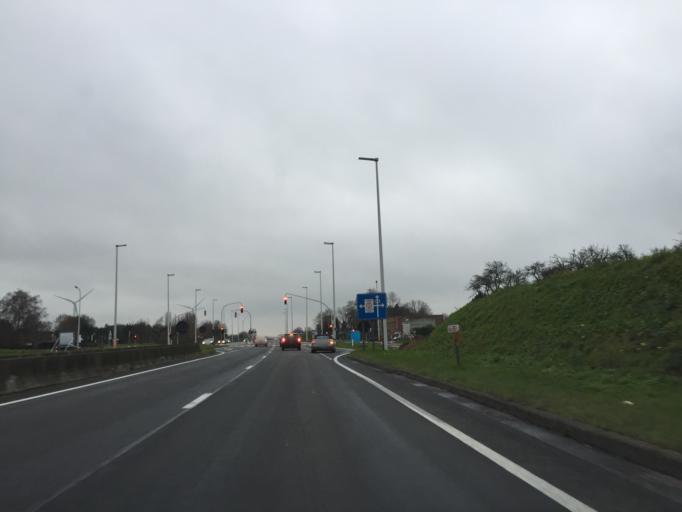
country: BE
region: Flanders
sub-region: Provincie Oost-Vlaanderen
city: Assenede
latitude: 51.1784
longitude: 3.7580
